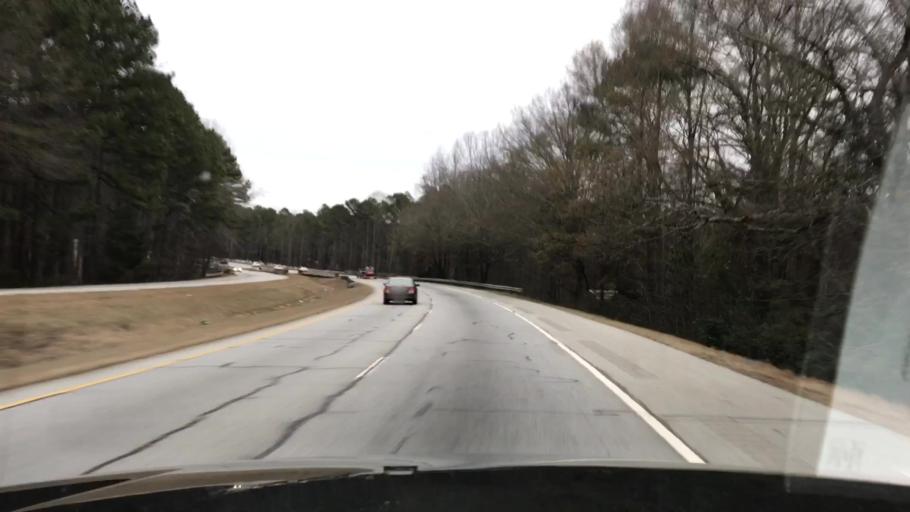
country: US
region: Georgia
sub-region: Walton County
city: Monroe
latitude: 33.8041
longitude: -83.6988
